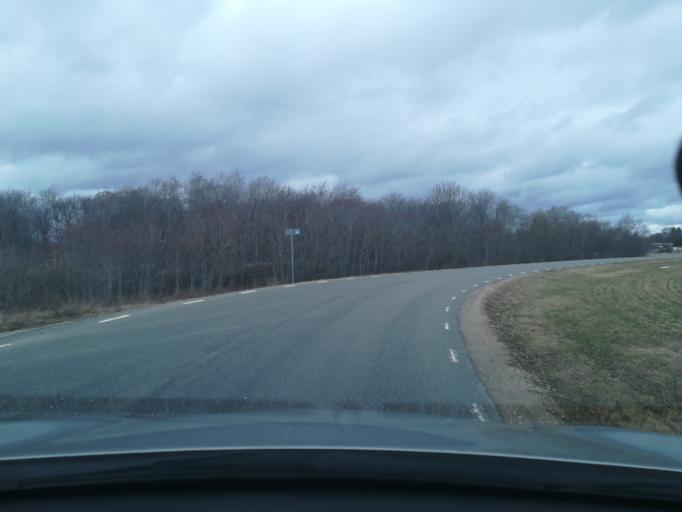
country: EE
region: Harju
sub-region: Saue linn
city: Saue
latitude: 59.3483
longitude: 24.5384
